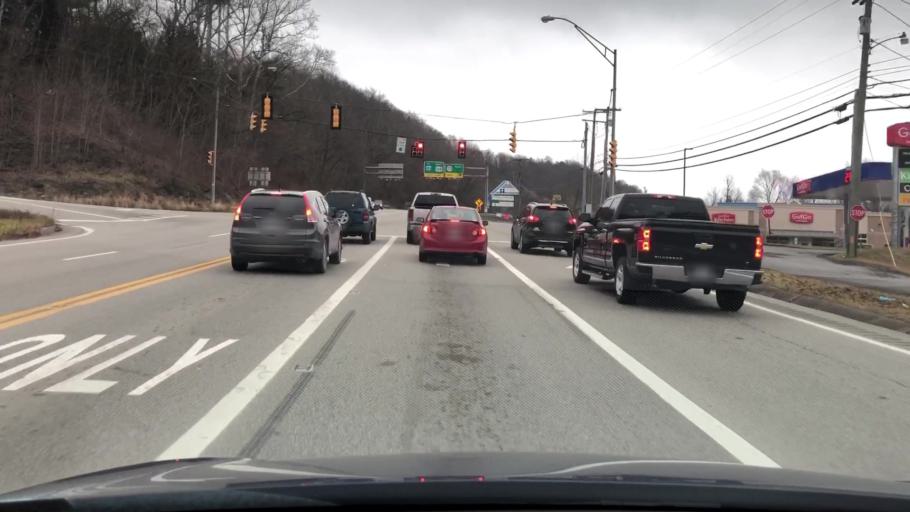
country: US
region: West Virginia
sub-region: Monongalia County
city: Morgantown
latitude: 39.6054
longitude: -79.9674
